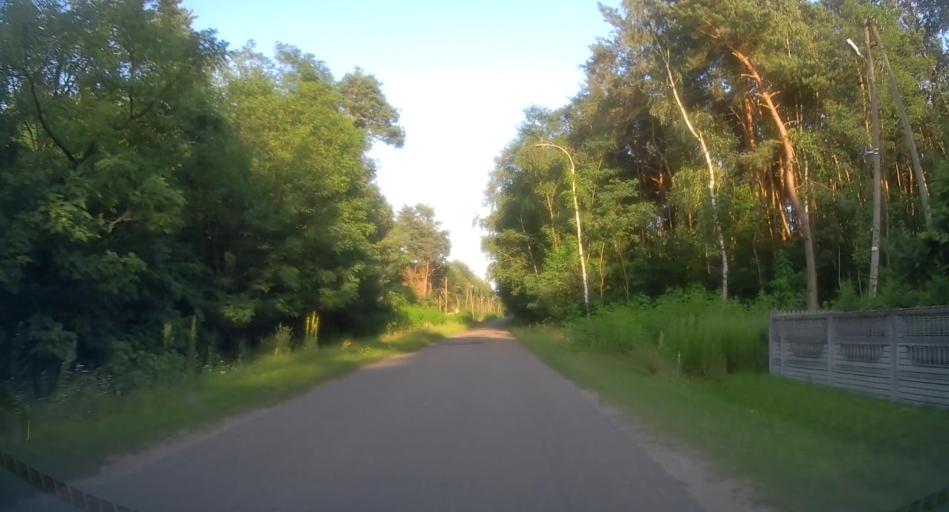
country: PL
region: Lodz Voivodeship
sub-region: Powiat skierniewicki
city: Kowiesy
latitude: 51.9055
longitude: 20.3532
